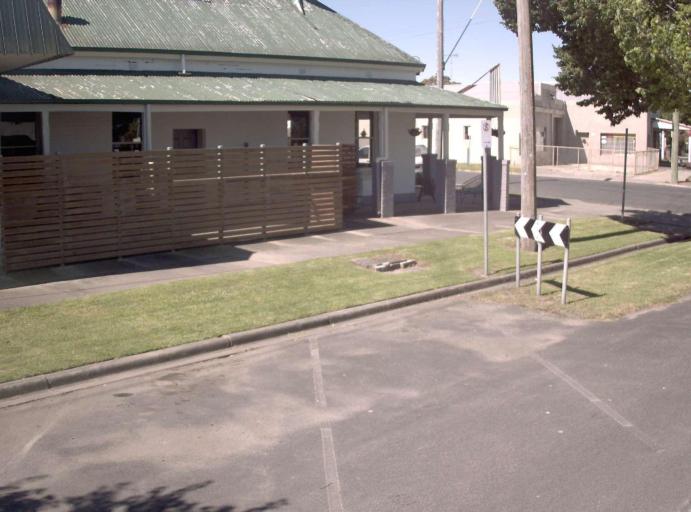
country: AU
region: Victoria
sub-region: Latrobe
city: Morwell
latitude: -38.6655
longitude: 146.4374
